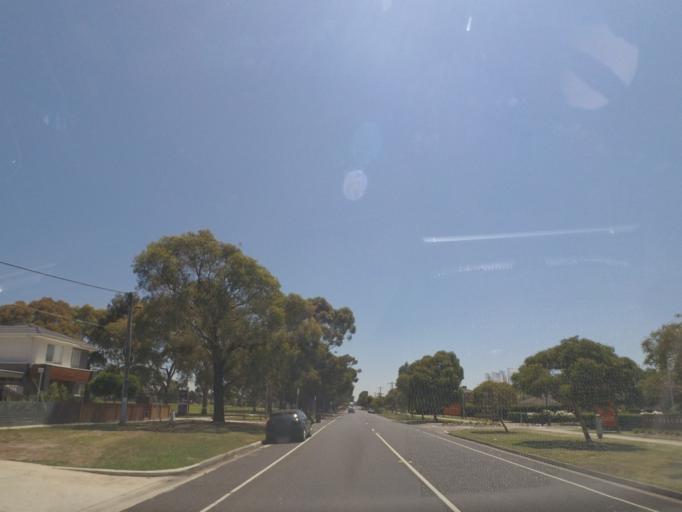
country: AU
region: Victoria
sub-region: Moreland
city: Hadfield
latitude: -37.7176
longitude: 144.9470
